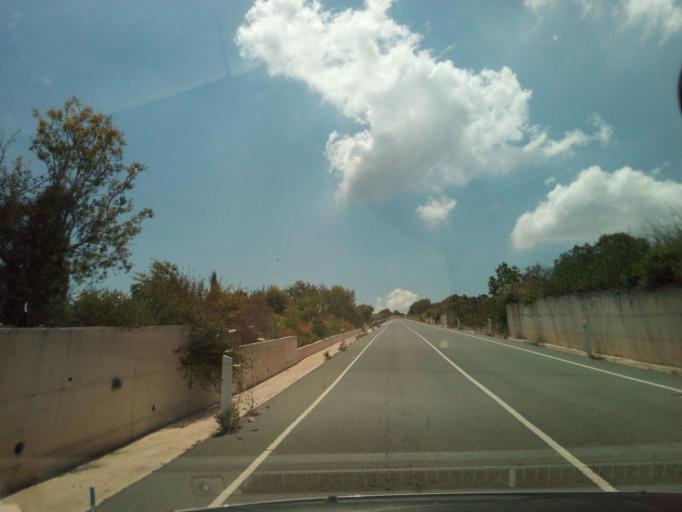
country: CY
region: Pafos
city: Tala
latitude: 34.9317
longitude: 32.5194
